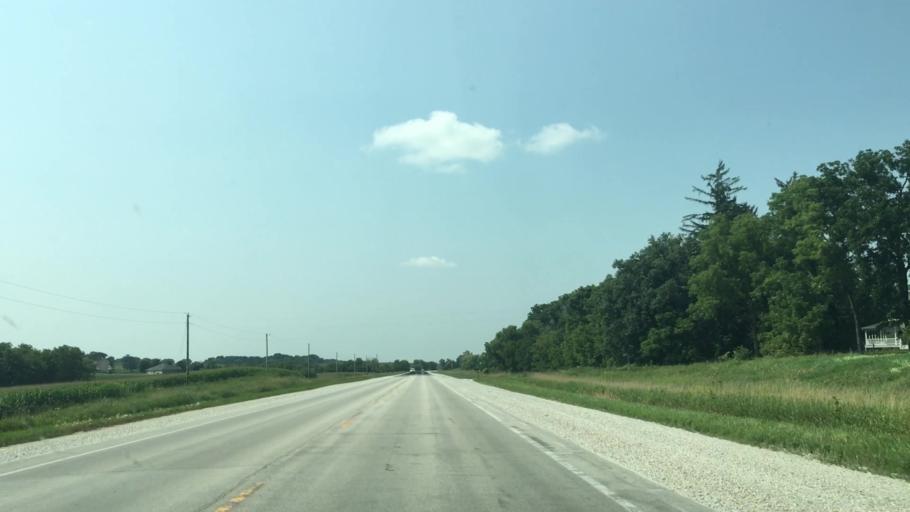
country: US
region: Iowa
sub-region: Winneshiek County
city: Decorah
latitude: 43.4007
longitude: -91.8451
